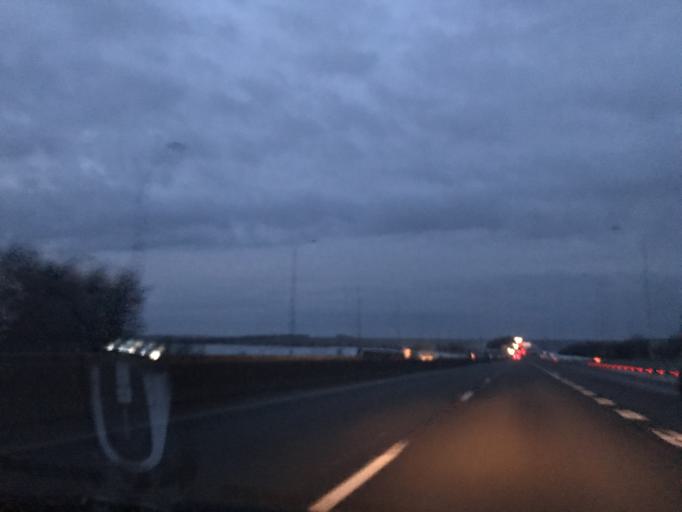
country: RU
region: Rostov
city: Samarskoye
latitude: 47.0047
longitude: 39.7313
